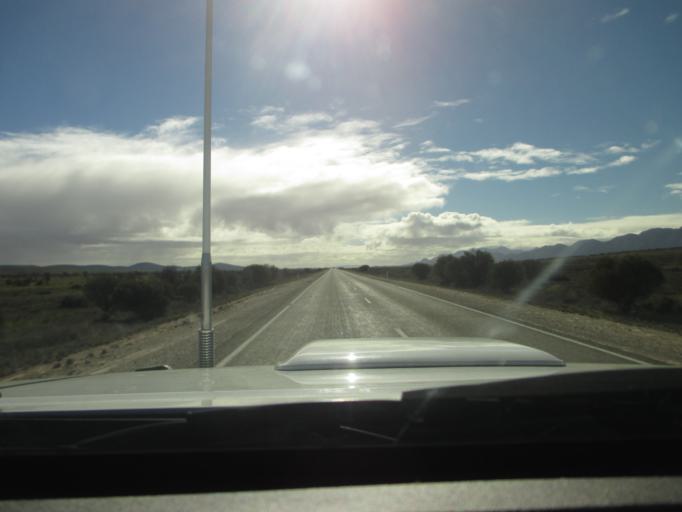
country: AU
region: South Australia
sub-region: Flinders Ranges
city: Quorn
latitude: -31.7123
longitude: 138.3515
